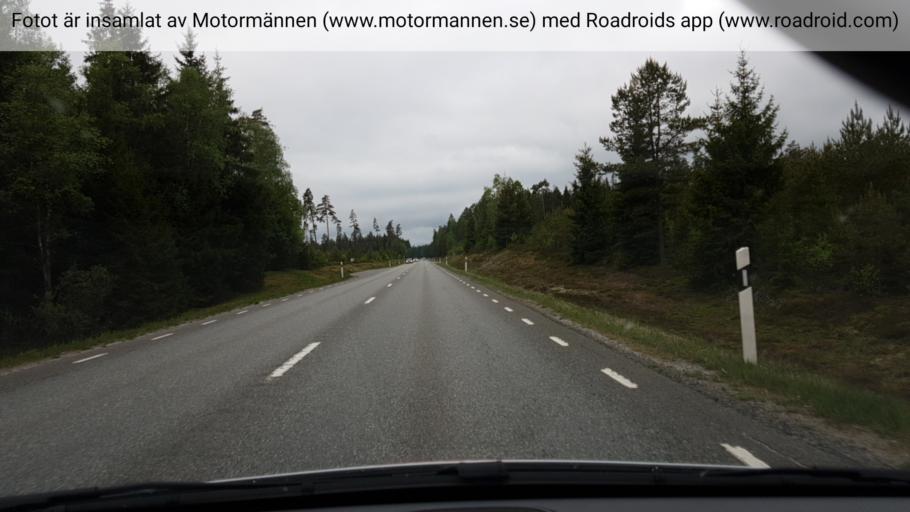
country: SE
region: Joenkoeping
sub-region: Gnosjo Kommun
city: Marieholm
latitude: 57.6369
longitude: 13.7928
